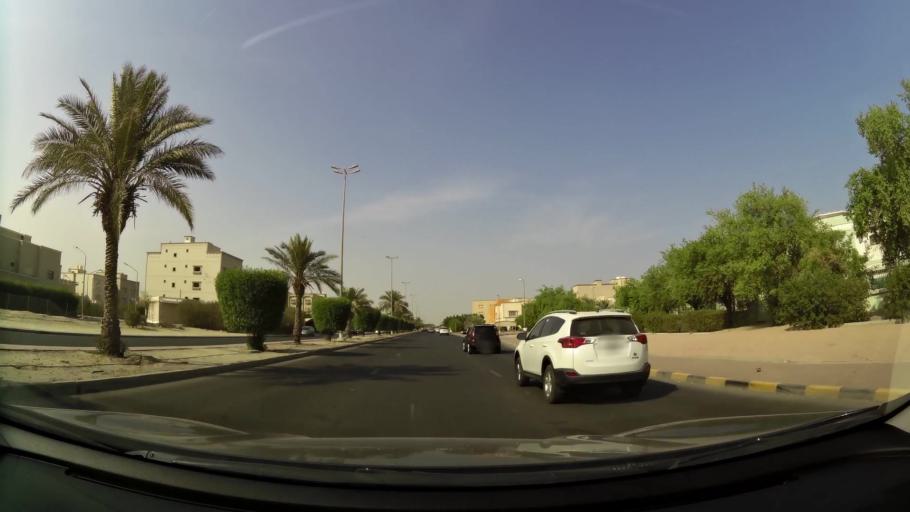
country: KW
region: Mubarak al Kabir
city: Mubarak al Kabir
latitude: 29.1712
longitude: 48.0853
